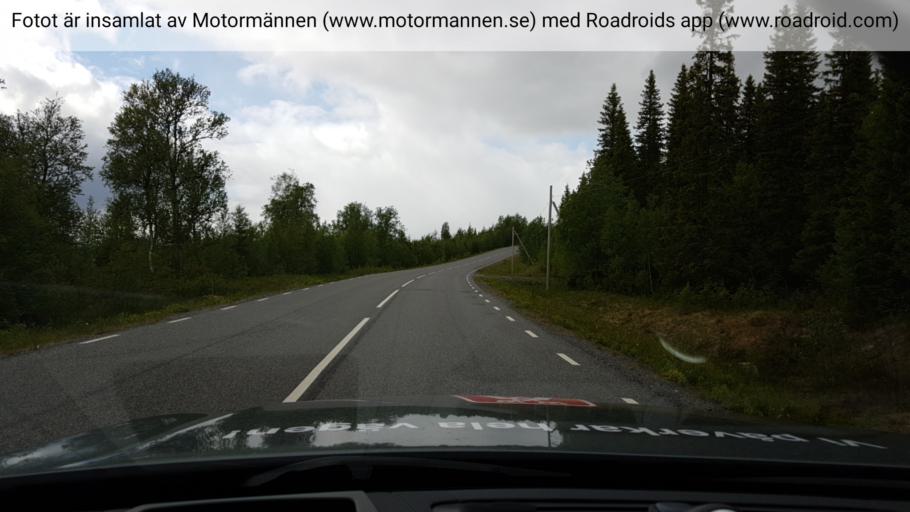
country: SE
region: Jaemtland
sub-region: Are Kommun
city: Are
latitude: 63.6413
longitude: 13.0805
